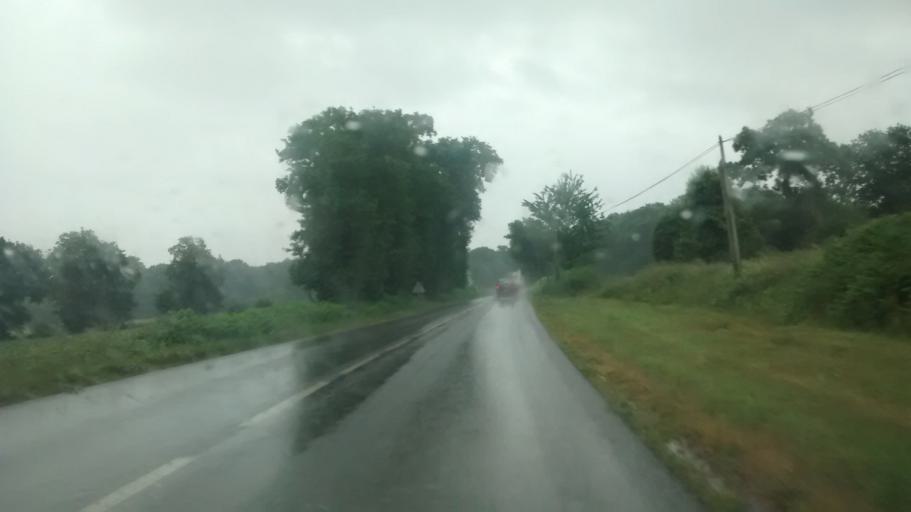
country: FR
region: Brittany
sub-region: Departement du Morbihan
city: La Gacilly
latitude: 47.7801
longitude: -2.1675
